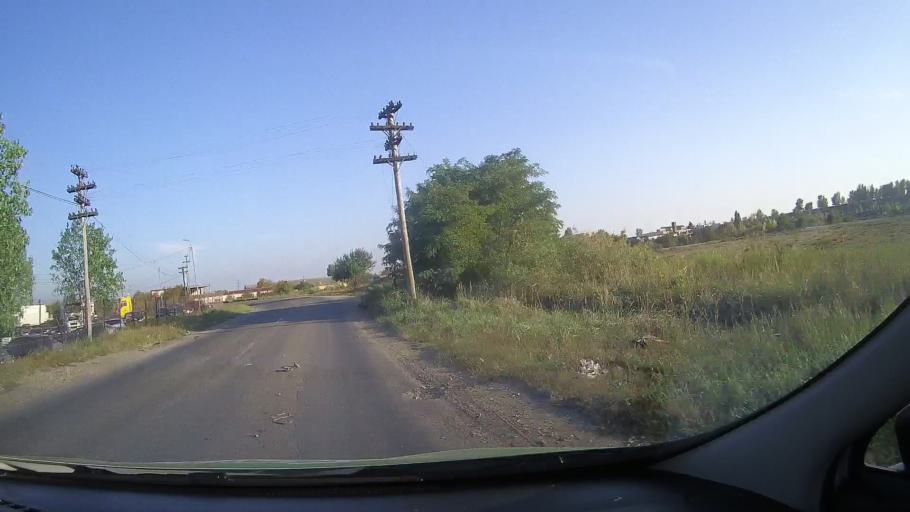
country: RO
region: Bihor
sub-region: Comuna Bors
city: Santion
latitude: 47.1039
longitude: 21.8747
